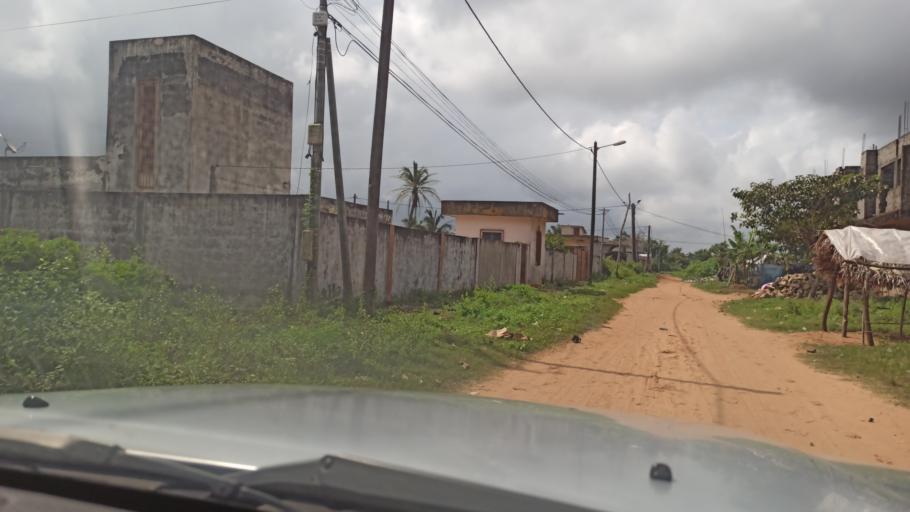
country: BJ
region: Queme
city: Porto-Novo
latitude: 6.4666
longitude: 2.6458
